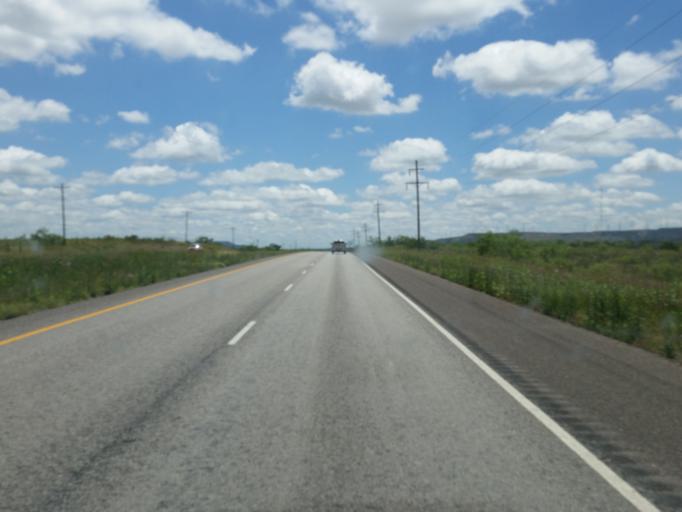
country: US
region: Texas
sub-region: Garza County
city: Post
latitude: 33.0010
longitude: -101.1601
